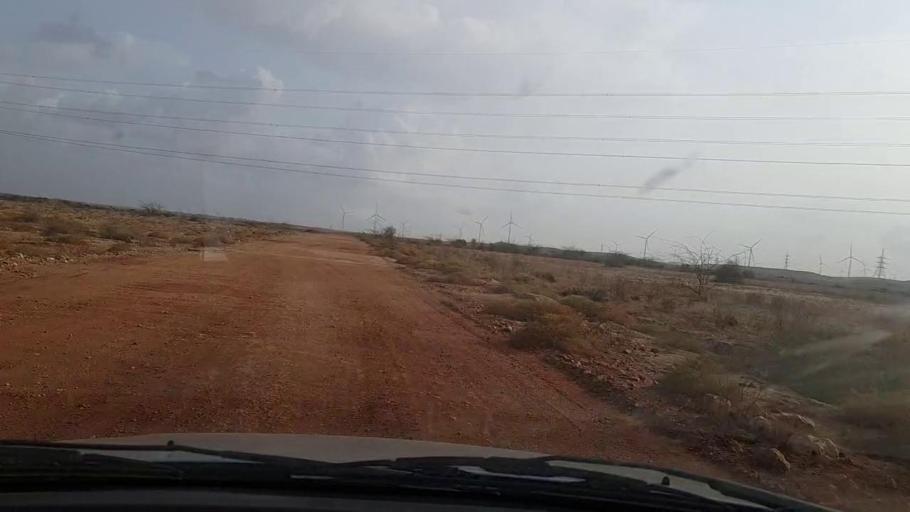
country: PK
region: Sindh
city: Thatta
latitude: 25.0592
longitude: 67.8827
